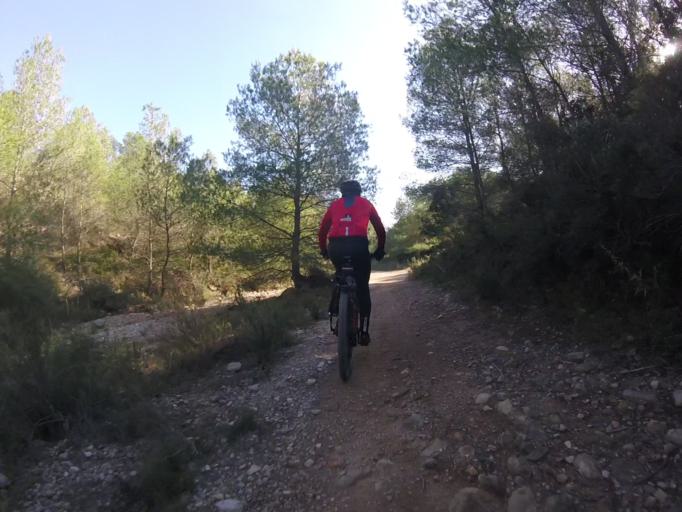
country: ES
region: Valencia
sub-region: Provincia de Castello
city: Santa Magdalena de Pulpis
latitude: 40.3056
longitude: 0.3388
